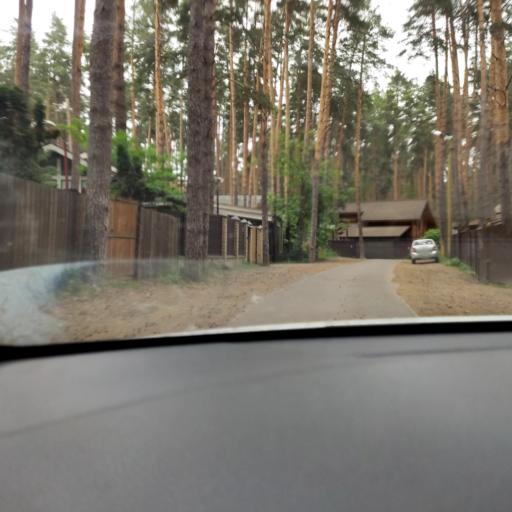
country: RU
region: Tatarstan
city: Verkhniy Uslon
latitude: 55.6456
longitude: 49.0233
